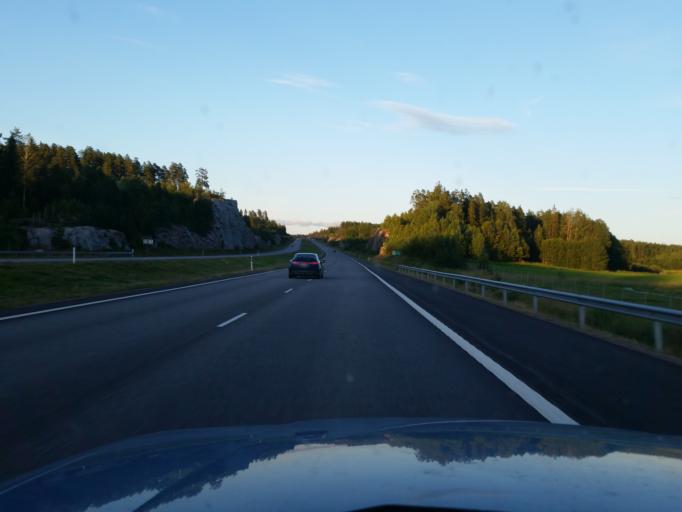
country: FI
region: Varsinais-Suomi
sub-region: Loimaa
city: Marttila
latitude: 60.4282
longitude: 22.8538
